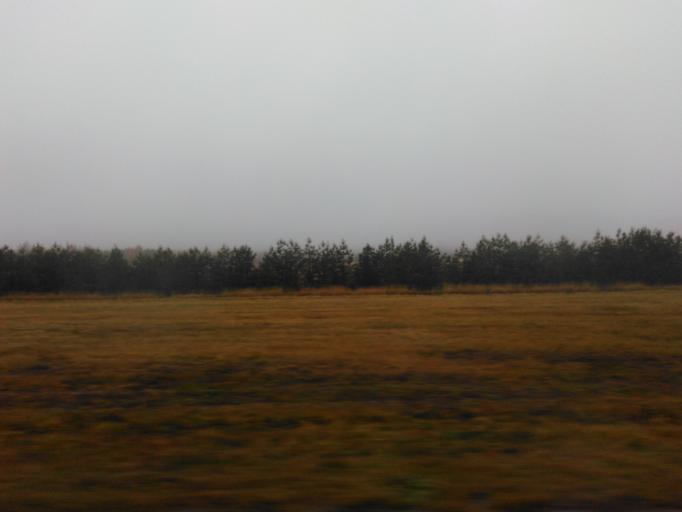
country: RU
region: Tatarstan
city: Sviyazhsk
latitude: 55.7350
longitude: 48.7792
